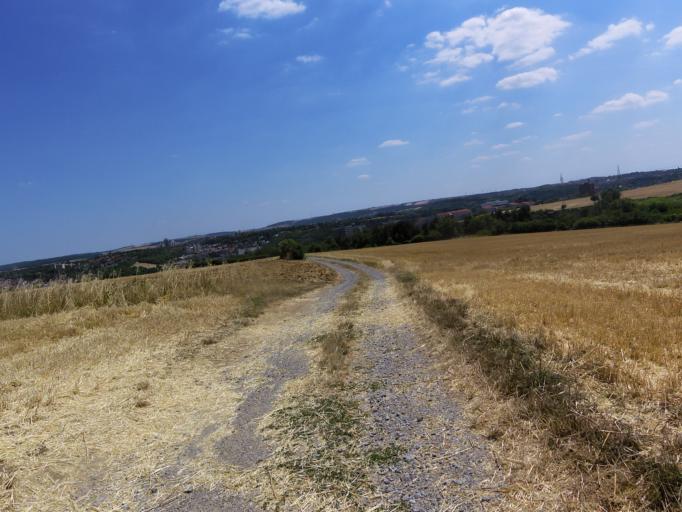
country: DE
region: Bavaria
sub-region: Regierungsbezirk Unterfranken
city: Wuerzburg
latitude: 49.8164
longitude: 9.9526
